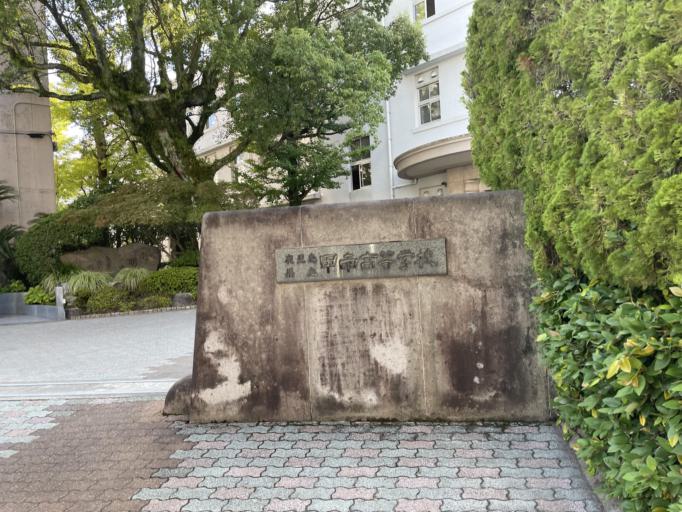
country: JP
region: Kagoshima
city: Kagoshima-shi
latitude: 31.5794
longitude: 130.5473
